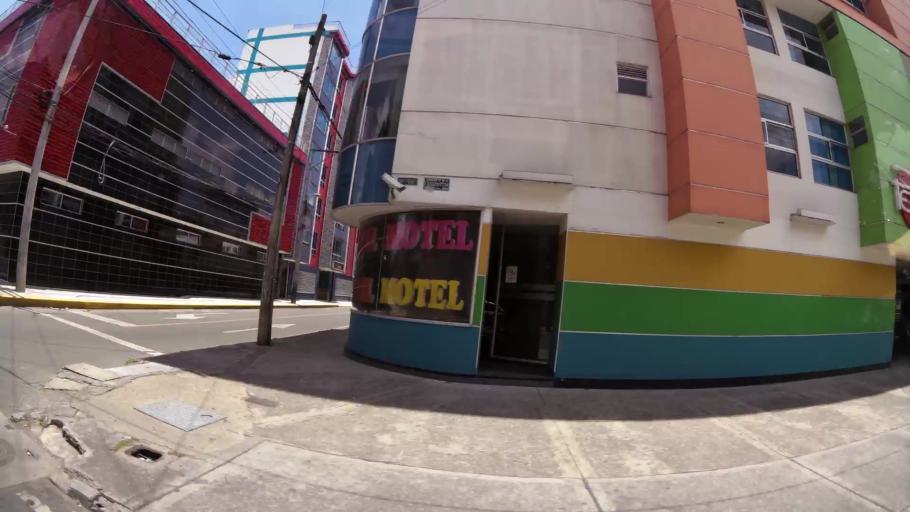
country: CO
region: Bogota D.C.
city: Bogota
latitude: 4.5844
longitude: -74.0992
